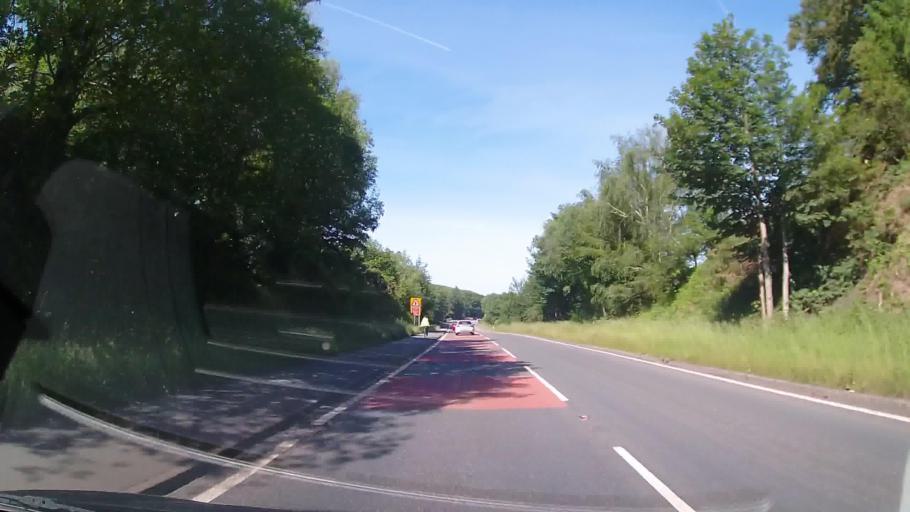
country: GB
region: Wales
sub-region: Sir Powys
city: Machynlleth
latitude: 52.5918
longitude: -3.8288
